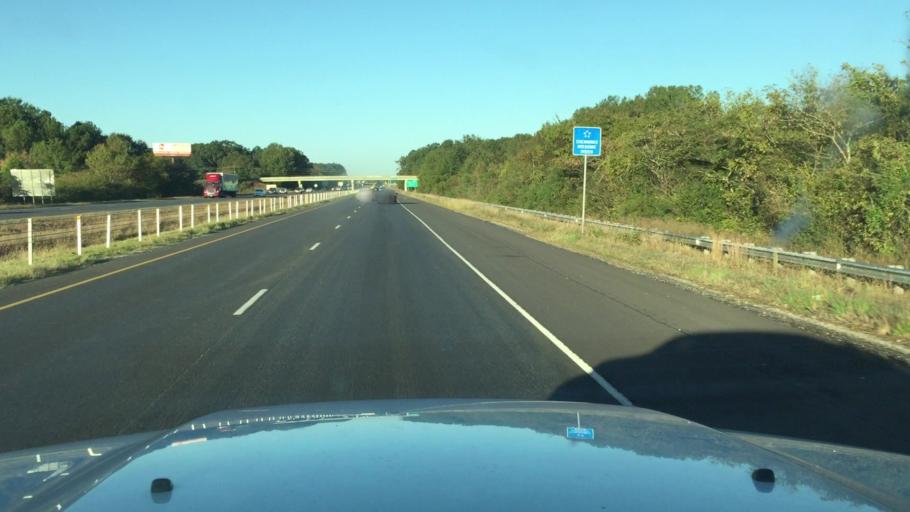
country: US
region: Alabama
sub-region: Etowah County
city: Gadsden
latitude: 33.9919
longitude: -86.0204
